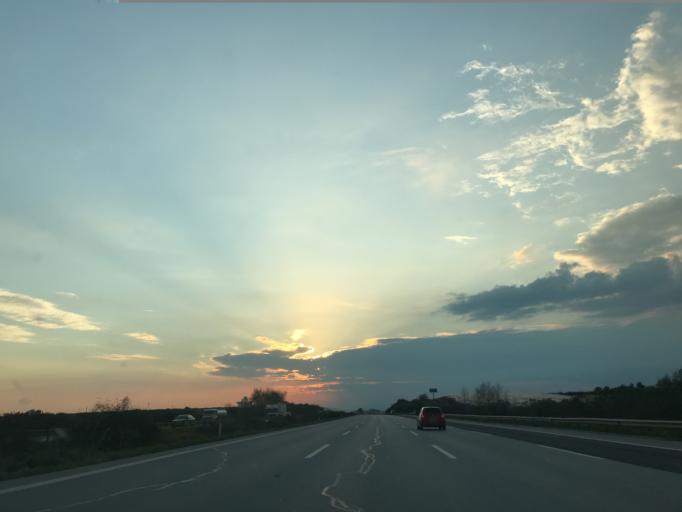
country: TR
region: Mersin
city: Yenice
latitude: 37.0225
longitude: 35.0451
